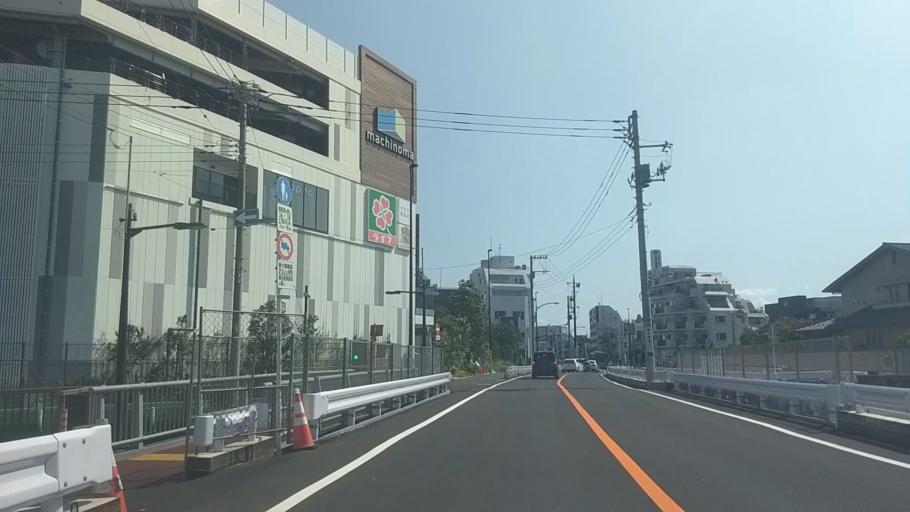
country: JP
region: Kanagawa
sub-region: Kawasaki-shi
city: Kawasaki
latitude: 35.5754
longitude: 139.7261
